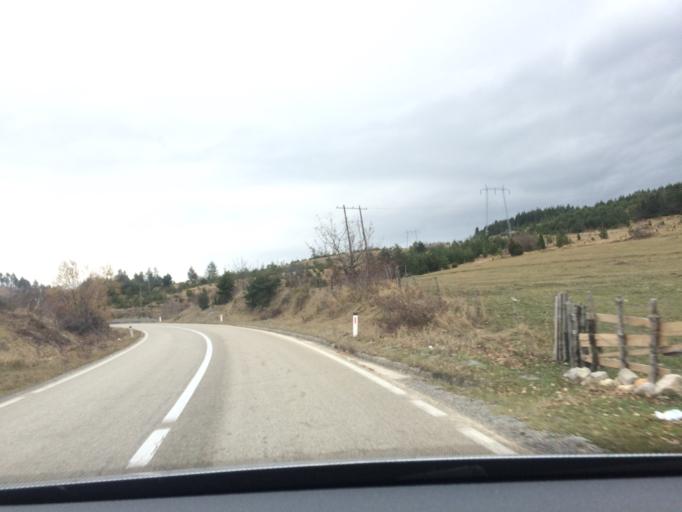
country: ME
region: Opstina Zabljak
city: Zabljak
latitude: 43.1476
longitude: 19.2472
